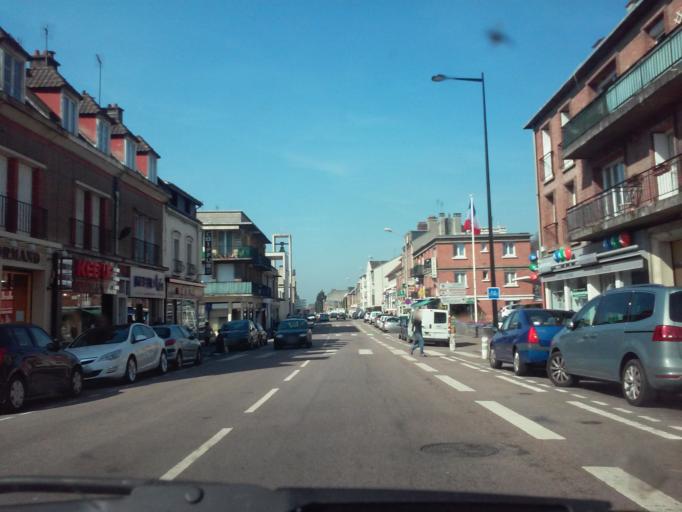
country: FR
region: Haute-Normandie
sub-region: Departement de la Seine-Maritime
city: Fontaine-la-Mallet
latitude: 49.5024
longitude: 0.1612
